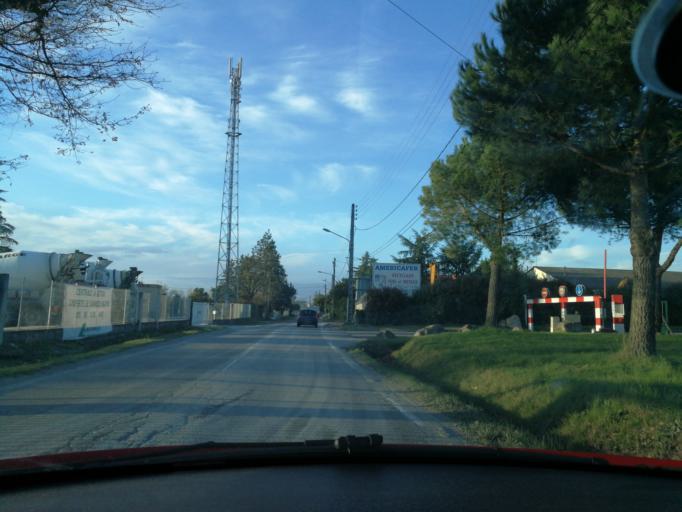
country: FR
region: Midi-Pyrenees
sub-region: Departement de la Haute-Garonne
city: Blagnac
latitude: 43.6485
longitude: 1.4138
